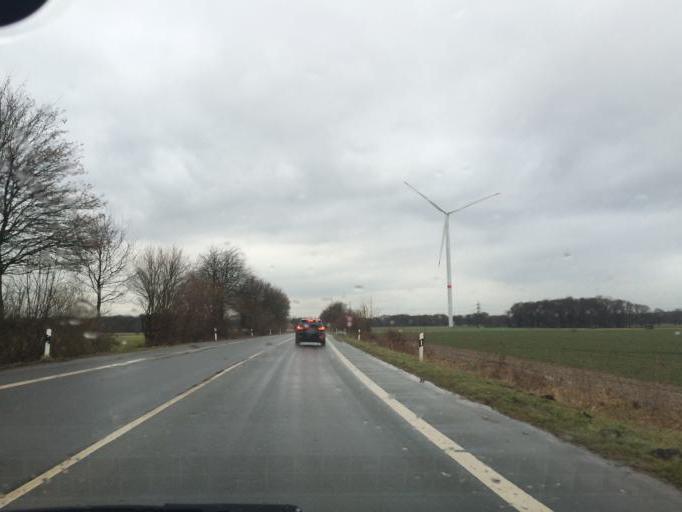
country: DE
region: North Rhine-Westphalia
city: Dorsten
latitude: 51.6185
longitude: 6.9532
